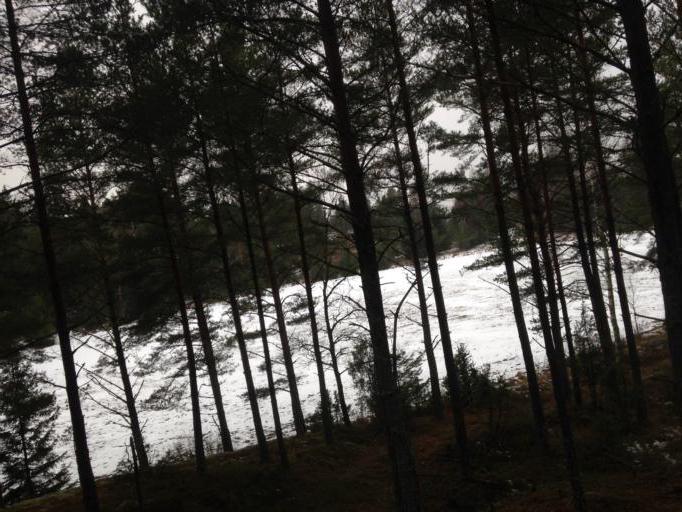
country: SE
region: OEstergoetland
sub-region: Norrkopings Kommun
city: Krokek
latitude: 58.5531
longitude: 16.5694
